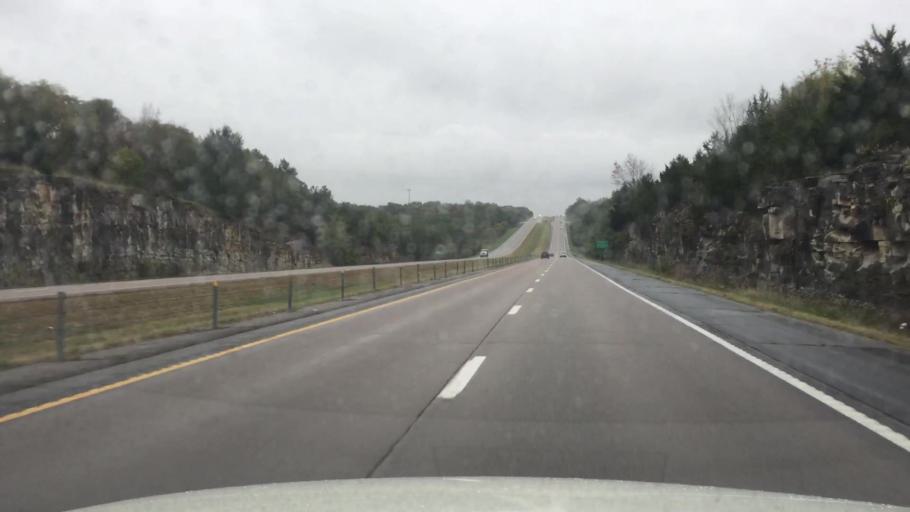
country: US
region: Missouri
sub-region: Boone County
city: Ashland
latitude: 38.7060
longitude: -92.2548
